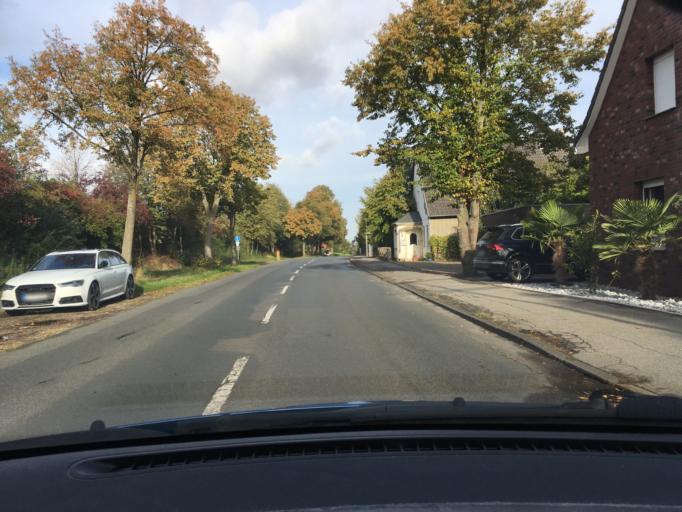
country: DE
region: Lower Saxony
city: Barsinghausen
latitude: 52.3157
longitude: 9.4367
